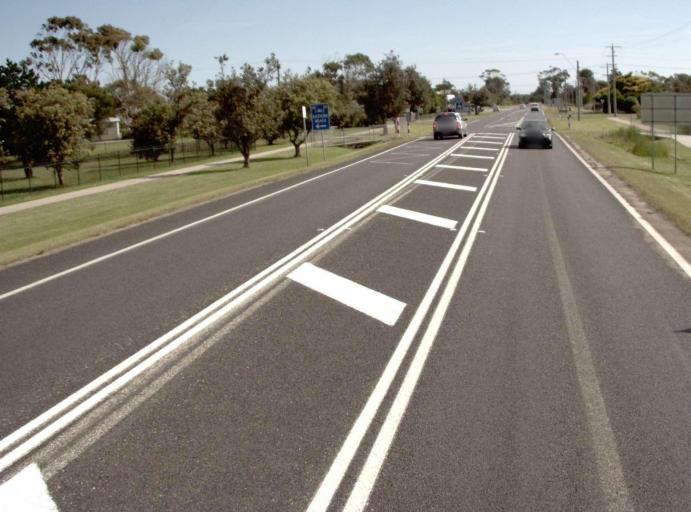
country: AU
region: Victoria
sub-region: East Gippsland
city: Lakes Entrance
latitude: -37.8720
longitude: 148.0102
